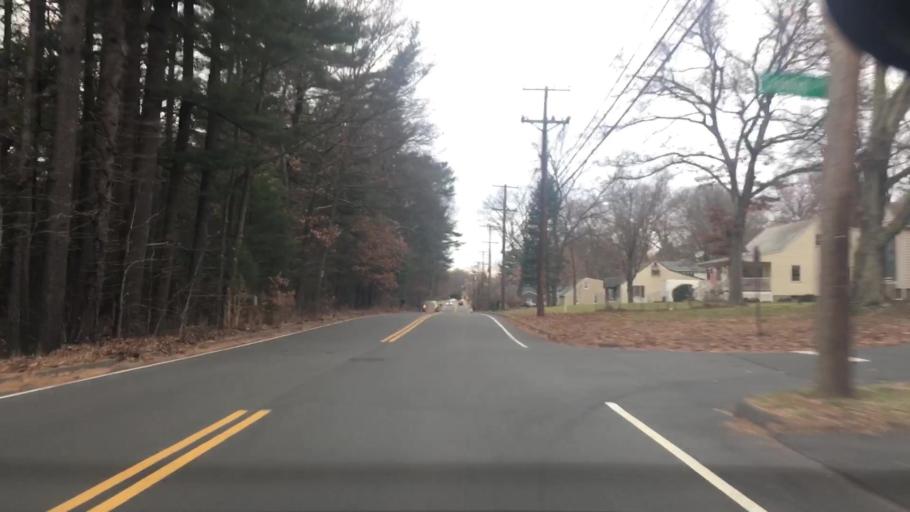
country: US
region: Connecticut
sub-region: Hartford County
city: Plainville
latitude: 41.6632
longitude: -72.9018
